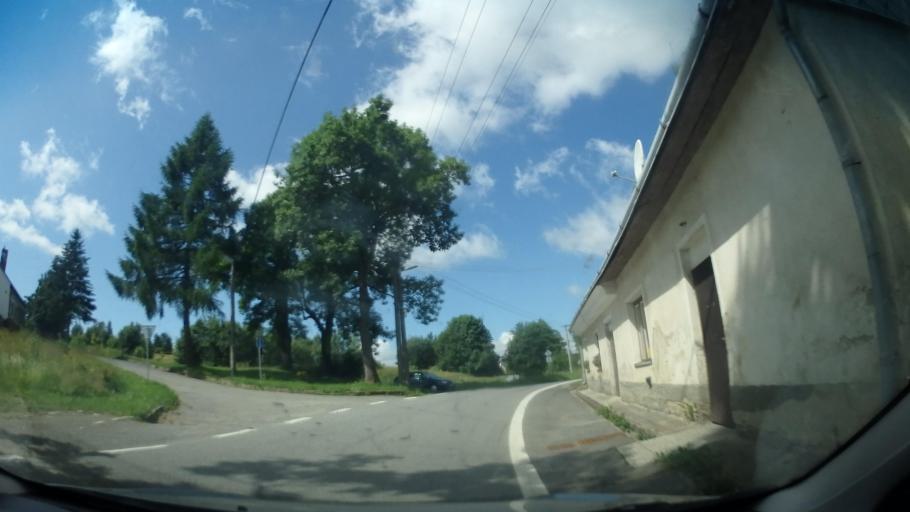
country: CZ
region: Vysocina
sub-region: Okres Zd'ar nad Sazavou
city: Nove Mesto na Morave
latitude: 49.6303
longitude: 16.0478
